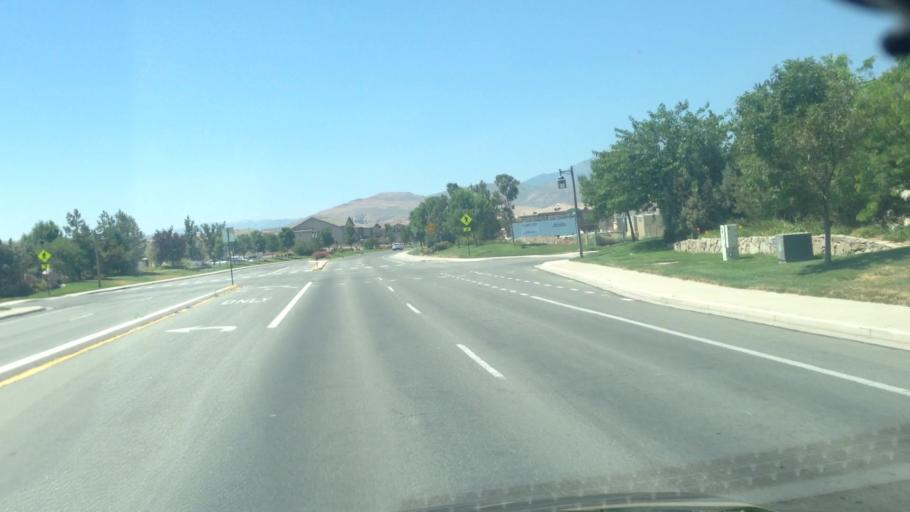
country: US
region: Nevada
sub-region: Washoe County
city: Sparks
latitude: 39.4273
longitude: -119.7263
